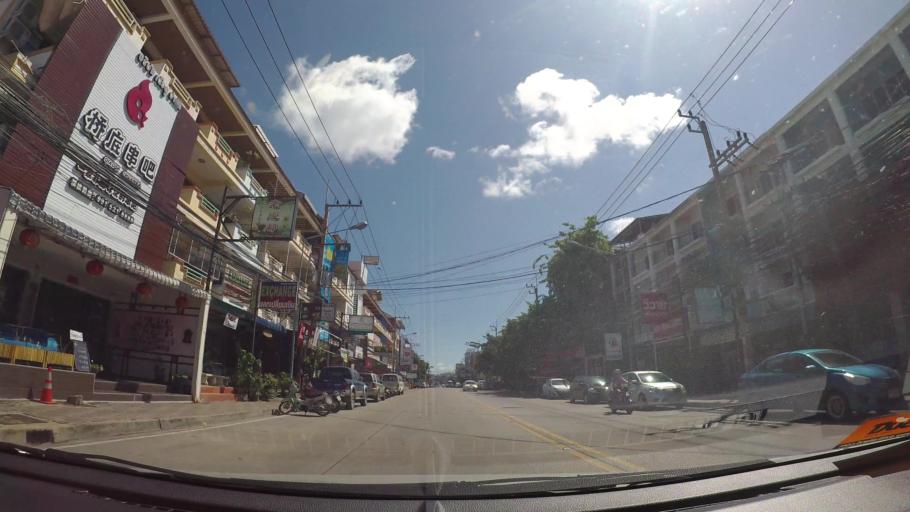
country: TH
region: Chon Buri
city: Phatthaya
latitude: 12.9368
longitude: 100.8930
